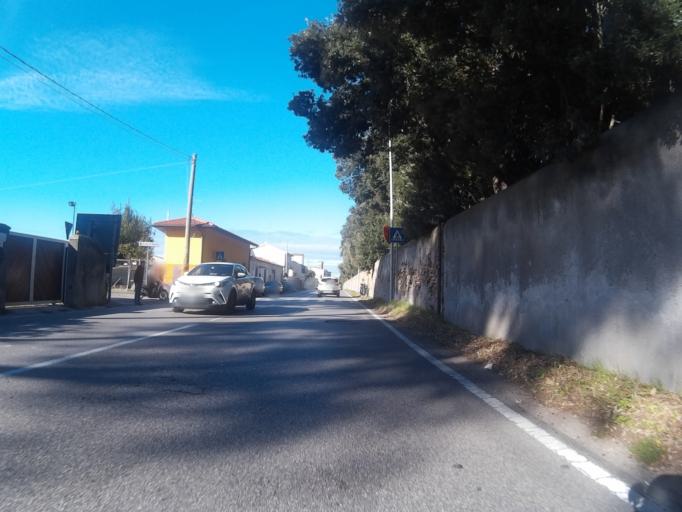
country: IT
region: Tuscany
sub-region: Provincia di Livorno
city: Livorno
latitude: 43.5109
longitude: 10.3302
